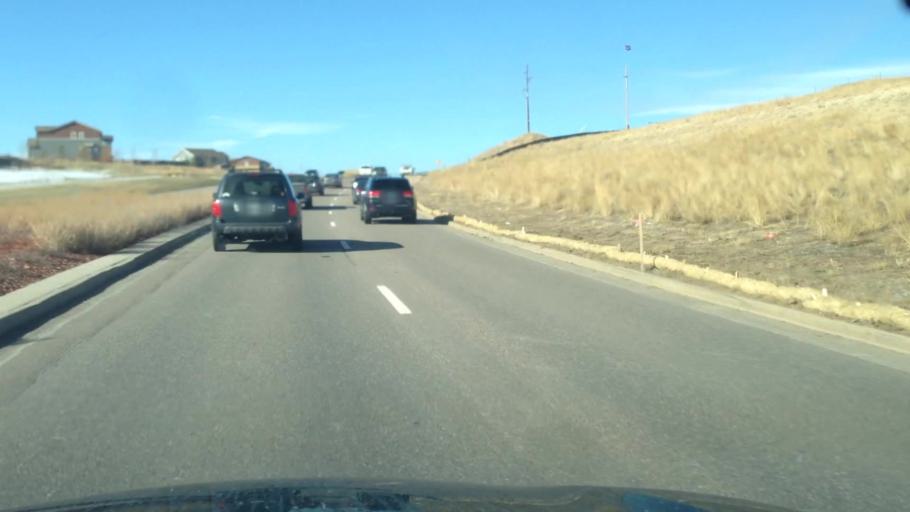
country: US
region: Colorado
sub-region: Douglas County
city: Stonegate
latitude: 39.5174
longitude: -104.8174
